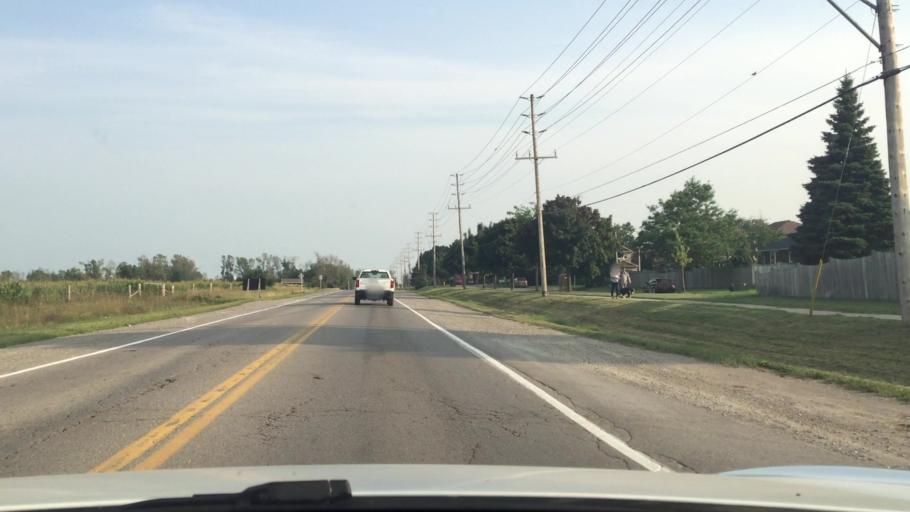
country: CA
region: Ontario
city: Oshawa
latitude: 43.9091
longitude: -78.7767
